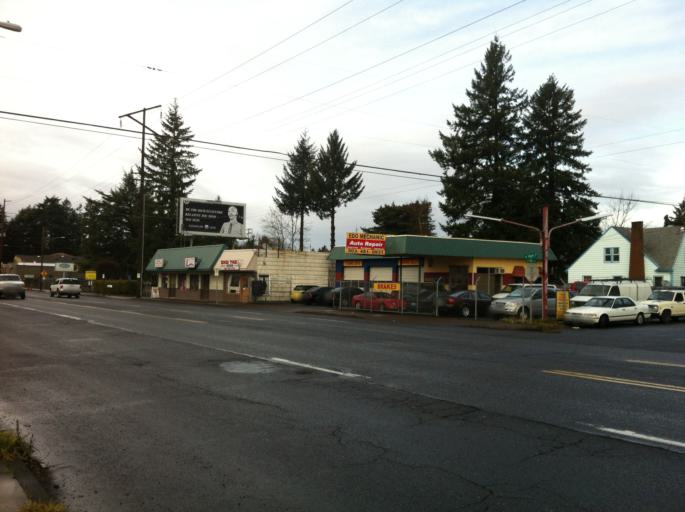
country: US
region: Oregon
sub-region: Multnomah County
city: Lents
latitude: 45.5190
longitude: -122.5183
